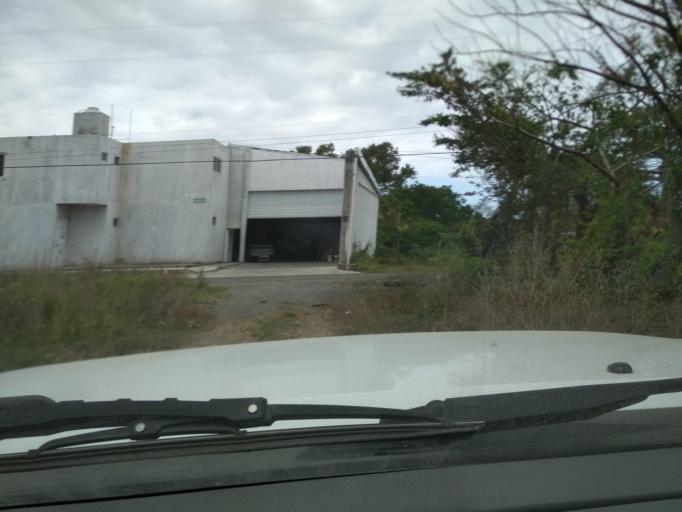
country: MX
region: Veracruz
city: El Tejar
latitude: 19.0736
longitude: -96.1492
